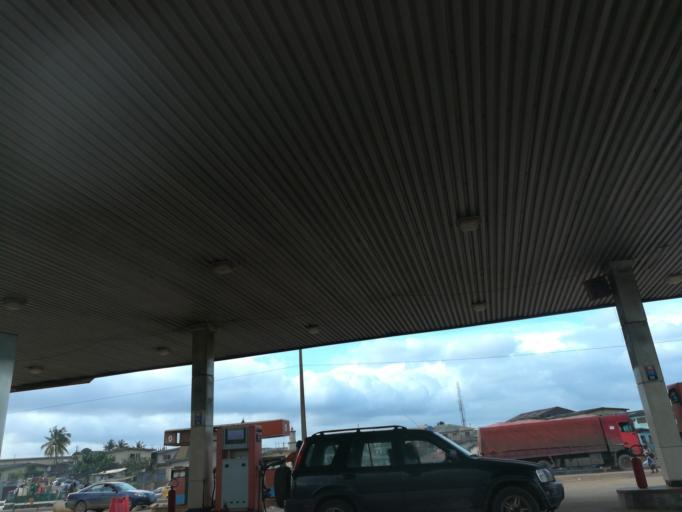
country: NG
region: Lagos
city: Agege
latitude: 6.6049
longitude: 3.3157
